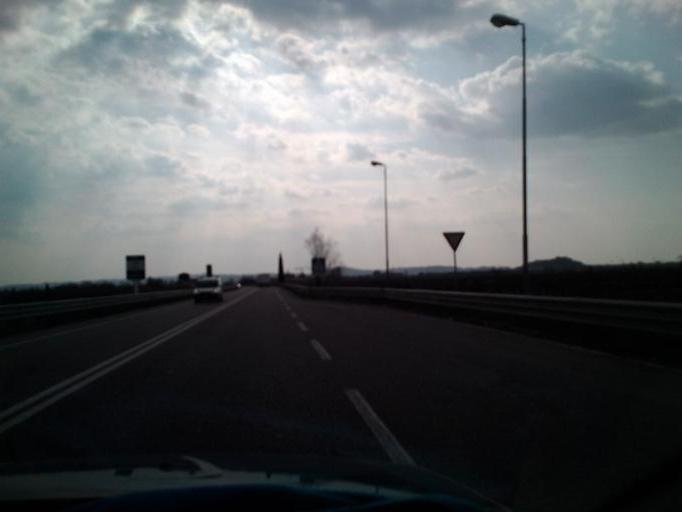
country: IT
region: Veneto
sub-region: Provincia di Verona
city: San Pietro in Cariano
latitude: 45.5192
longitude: 10.8723
